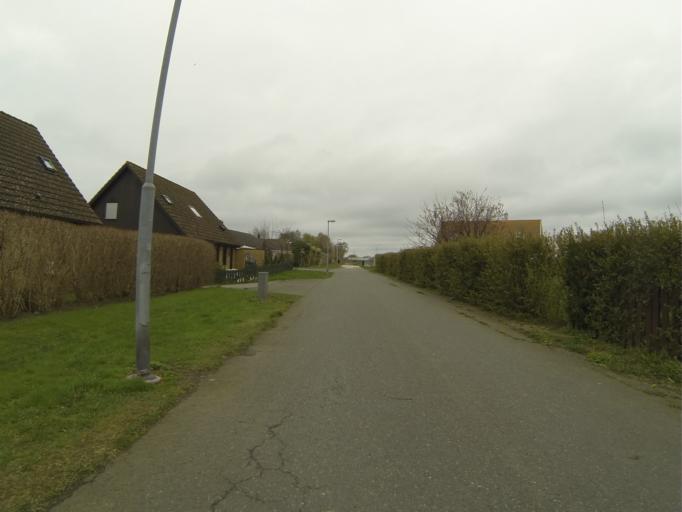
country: SE
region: Skane
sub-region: Simrishamns Kommun
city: Simrishamn
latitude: 55.5424
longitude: 14.3400
